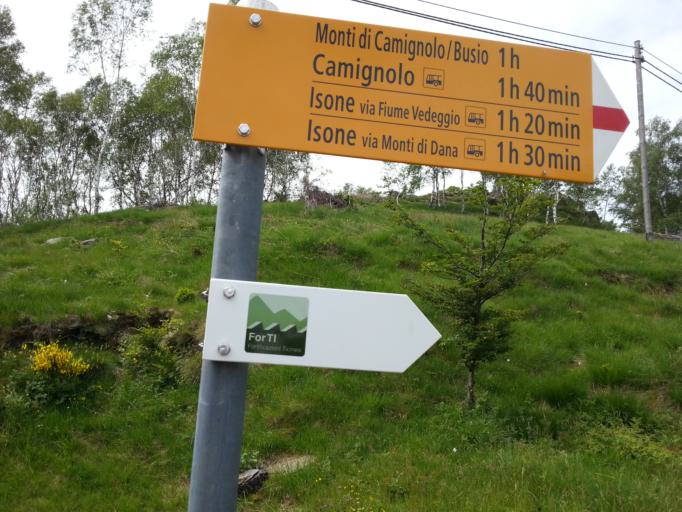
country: CH
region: Ticino
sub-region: Lugano District
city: Tesserete
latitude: 46.1029
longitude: 8.9651
